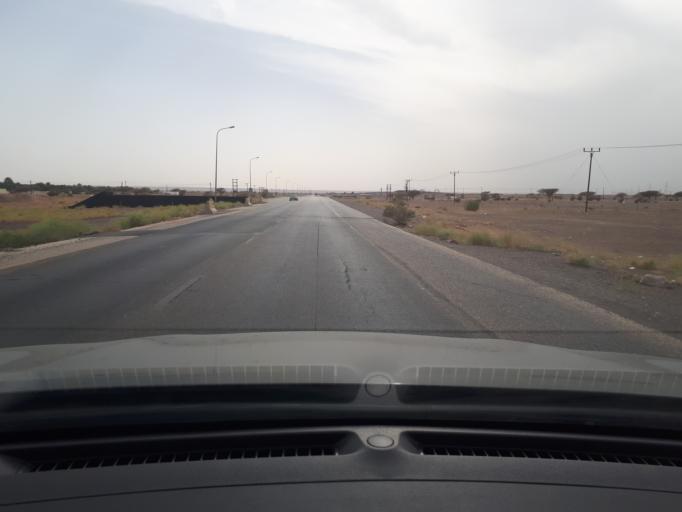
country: OM
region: Ash Sharqiyah
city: Badiyah
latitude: 22.4664
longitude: 58.8790
